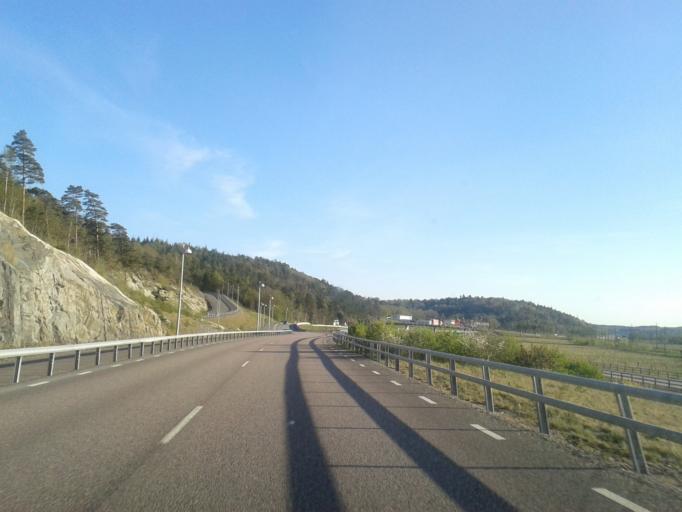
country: SE
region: Vaestra Goetaland
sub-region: Ale Kommun
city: Nodinge-Nol
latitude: 57.8802
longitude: 12.0389
